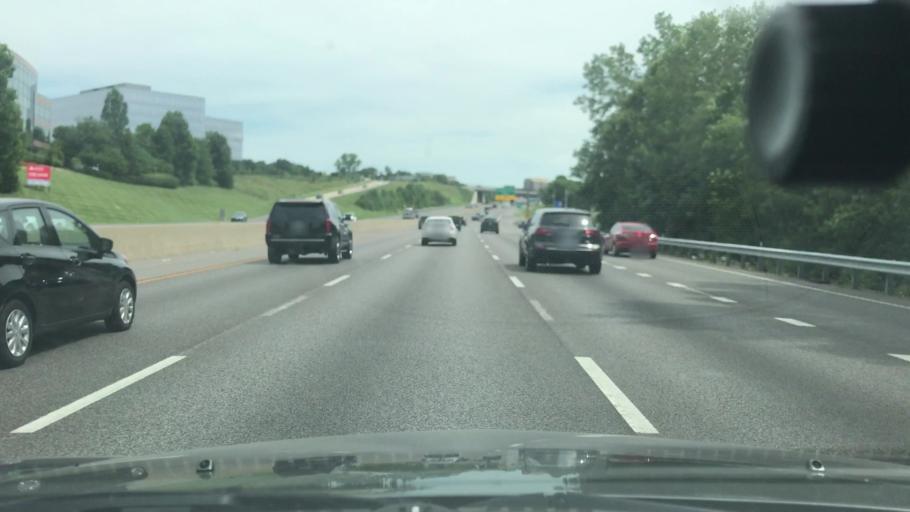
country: US
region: Missouri
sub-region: Saint Louis County
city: Chesterfield
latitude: 38.6631
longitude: -90.5711
